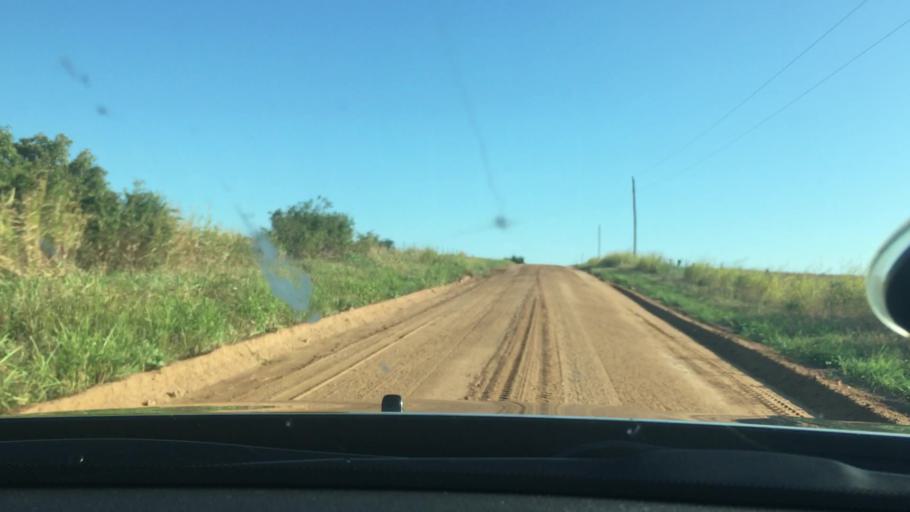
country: US
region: Oklahoma
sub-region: Murray County
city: Sulphur
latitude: 34.4159
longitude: -96.7935
